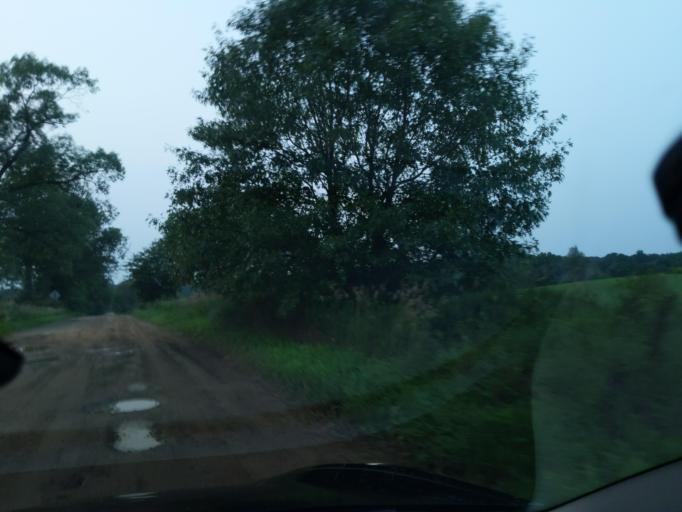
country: US
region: Michigan
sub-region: Ingham County
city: Leslie
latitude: 42.3431
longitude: -84.5122
